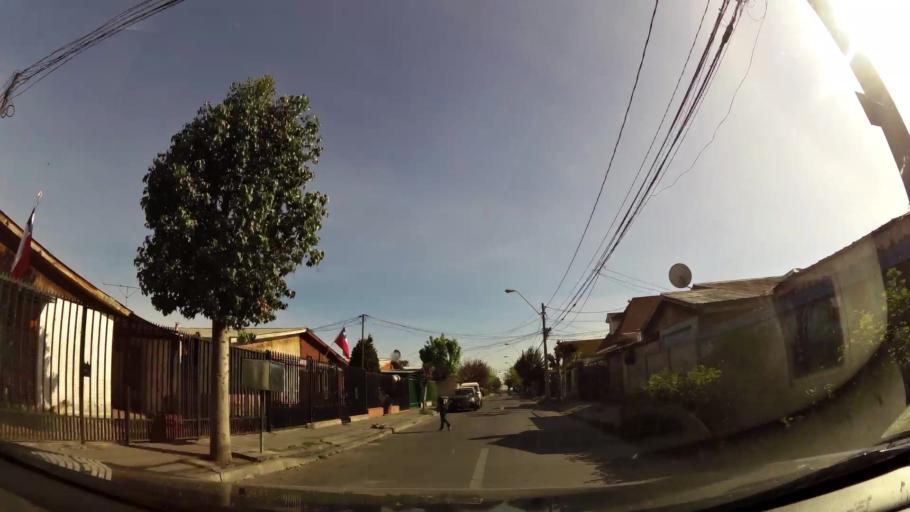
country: CL
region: Santiago Metropolitan
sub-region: Provincia de Cordillera
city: Puente Alto
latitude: -33.6090
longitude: -70.5990
